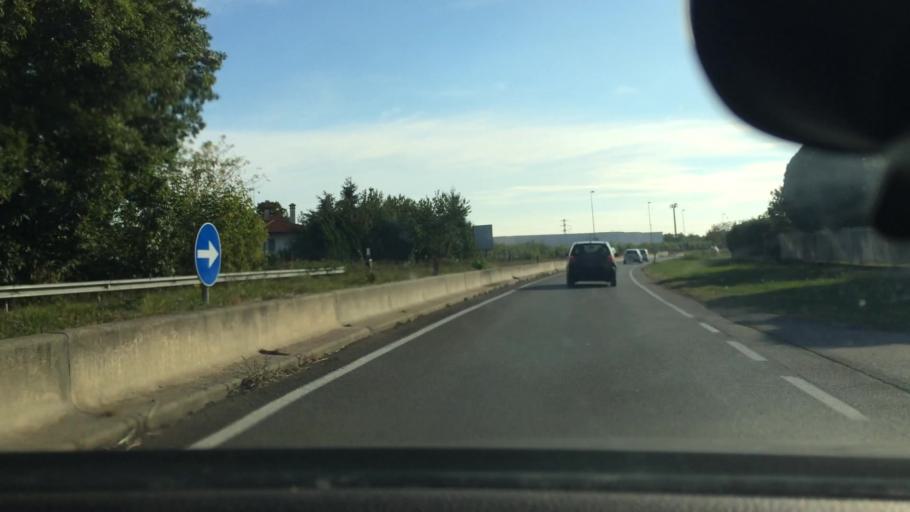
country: IT
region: Lombardy
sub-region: Citta metropolitana di Milano
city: Villa Cortese
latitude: 45.5634
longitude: 8.8956
